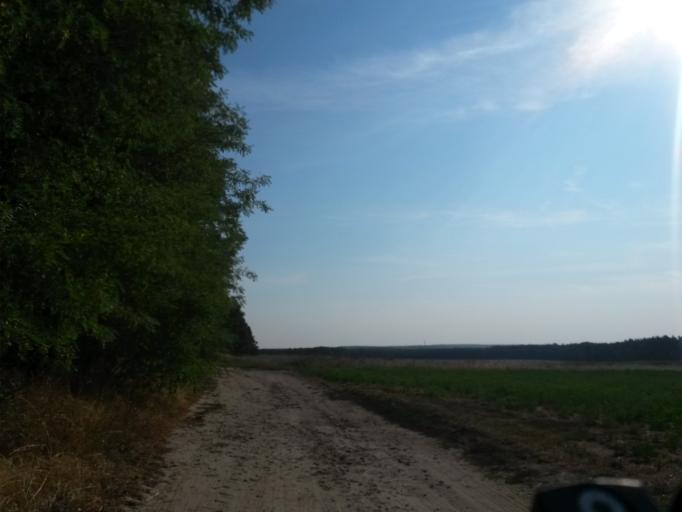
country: DE
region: Saxony-Anhalt
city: Nudersdorf
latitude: 51.9036
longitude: 12.5837
